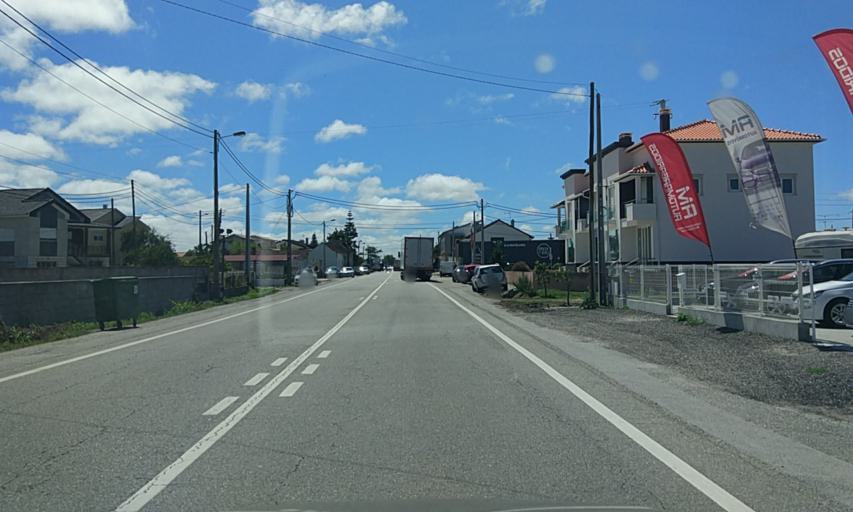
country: PT
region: Coimbra
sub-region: Mira
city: Mira
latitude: 40.4755
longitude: -8.6960
